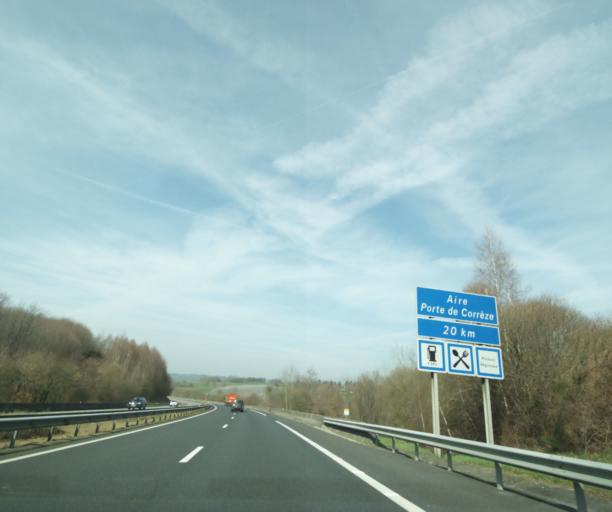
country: FR
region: Limousin
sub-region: Departement de la Correze
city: Uzerche
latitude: 45.4051
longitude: 1.5587
